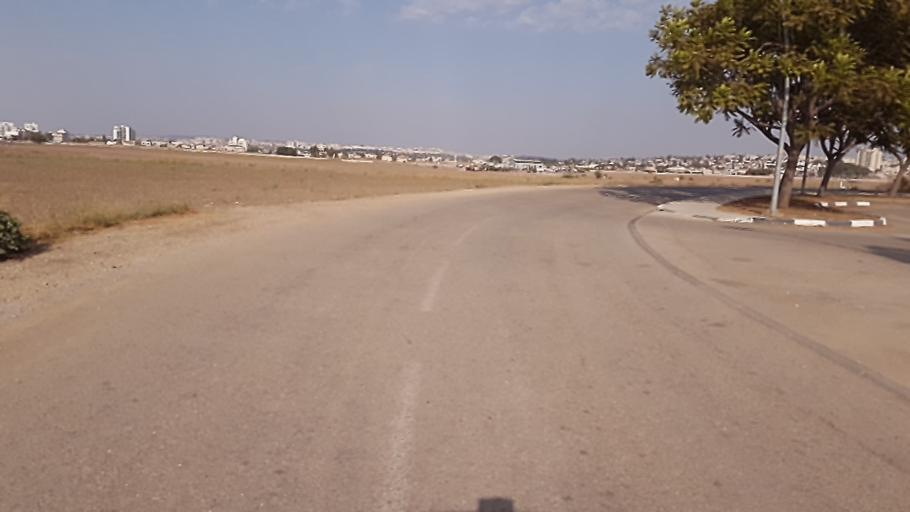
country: IL
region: Central District
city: Rosh Ha'Ayin
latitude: 32.0862
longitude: 34.9368
